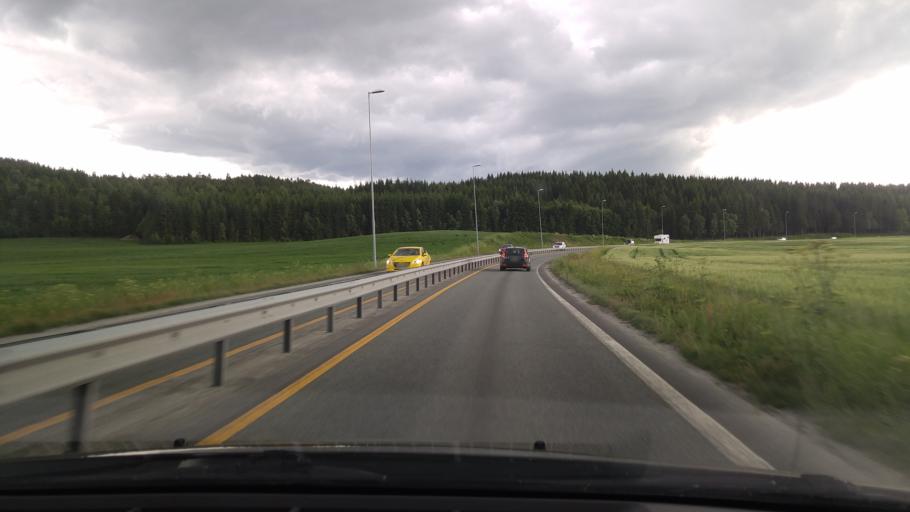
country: NO
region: Nord-Trondelag
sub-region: Levanger
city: Levanger
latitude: 63.7491
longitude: 11.3791
